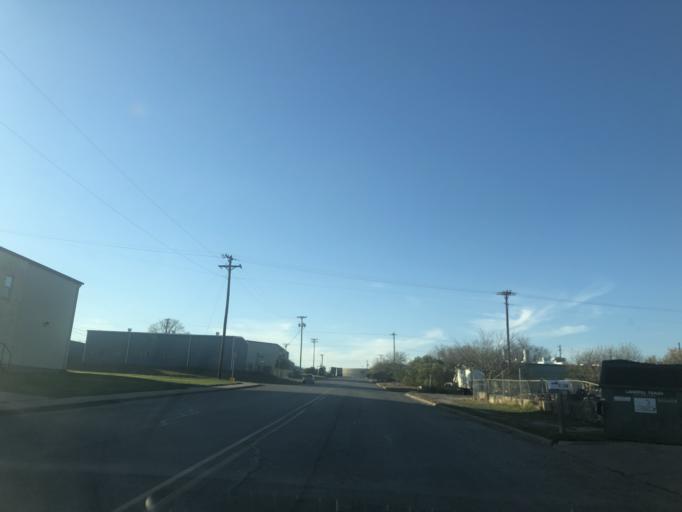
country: US
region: Texas
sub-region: Travis County
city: Wells Branch
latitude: 30.4314
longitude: -97.6793
